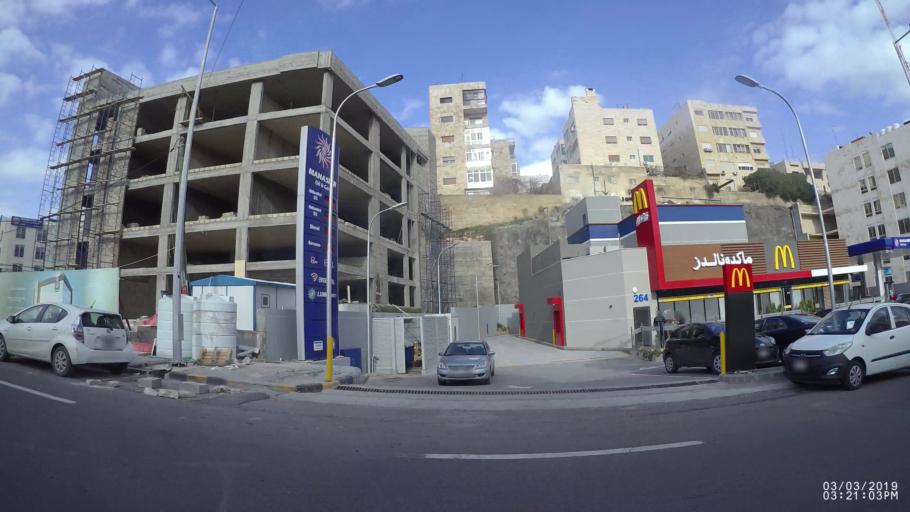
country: JO
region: Amman
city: Amman
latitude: 31.9643
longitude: 35.8882
